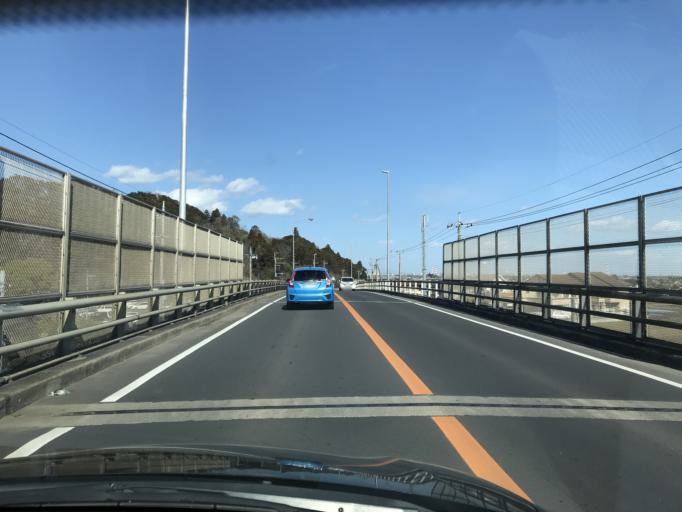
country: JP
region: Chiba
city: Omigawa
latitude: 35.8562
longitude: 140.5911
